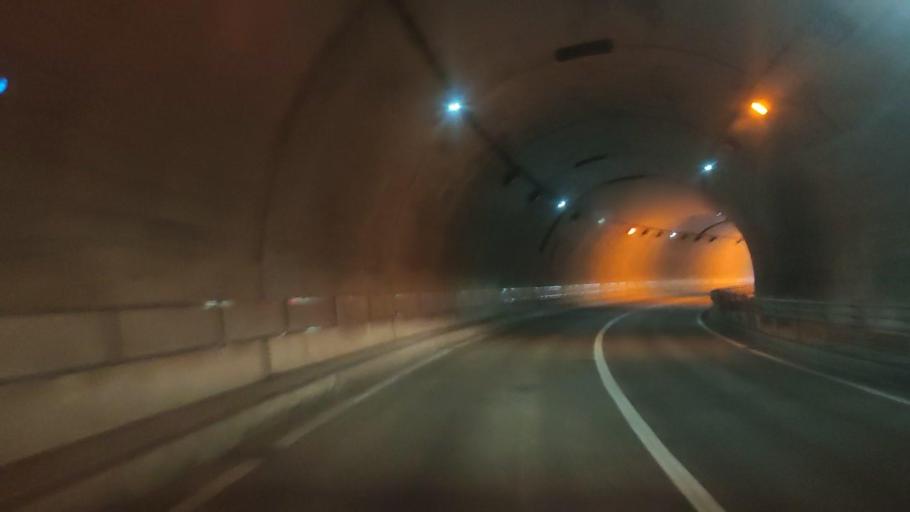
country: JP
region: Kagoshima
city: Kagoshima-shi
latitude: 31.5975
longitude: 130.5492
